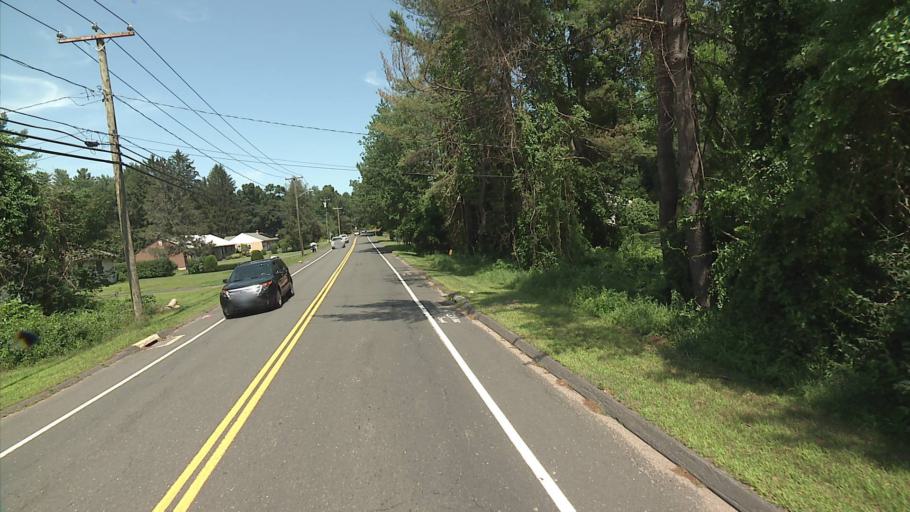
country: US
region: Connecticut
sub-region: Hartford County
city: Salmon Brook
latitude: 41.9540
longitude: -72.7989
